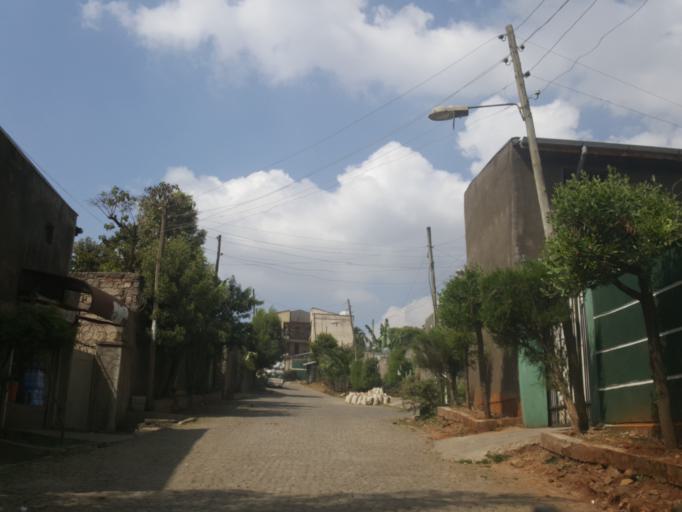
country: ET
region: Adis Abeba
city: Addis Ababa
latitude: 9.0572
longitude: 38.7206
